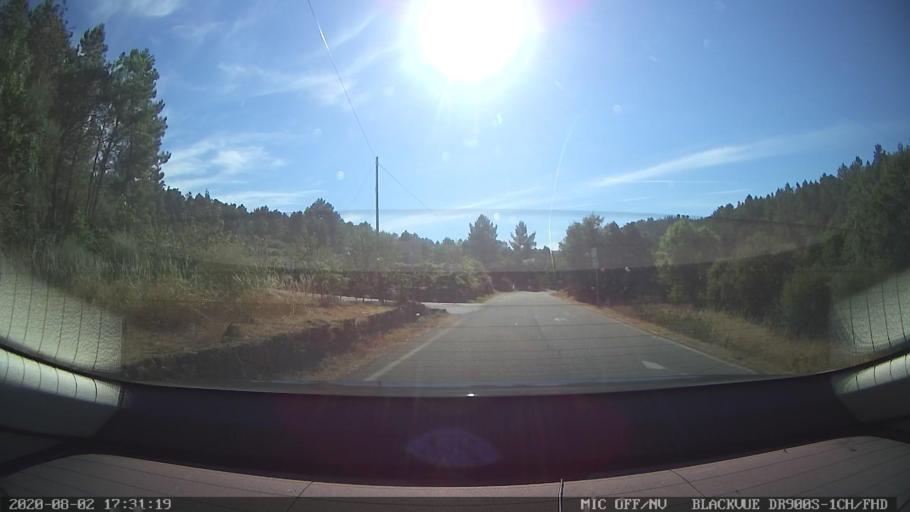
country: PT
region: Vila Real
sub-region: Sabrosa
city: Sabrosa
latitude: 41.3557
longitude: -7.5755
